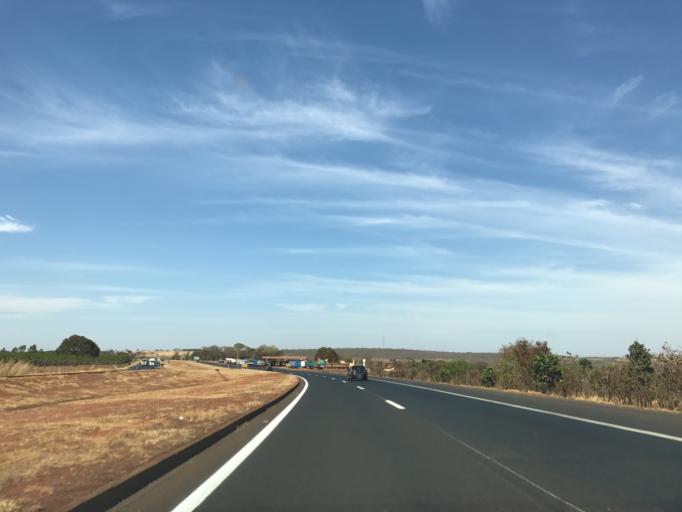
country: BR
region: Minas Gerais
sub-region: Monte Alegre De Minas
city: Monte Alegre de Minas
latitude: -18.8132
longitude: -49.0865
